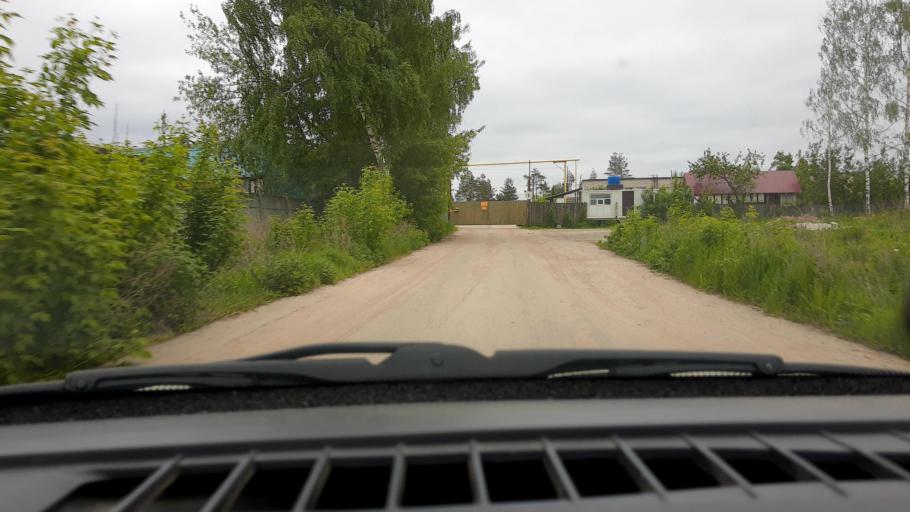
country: RU
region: Nizjnij Novgorod
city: Gorbatovka
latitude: 56.3346
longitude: 43.7985
